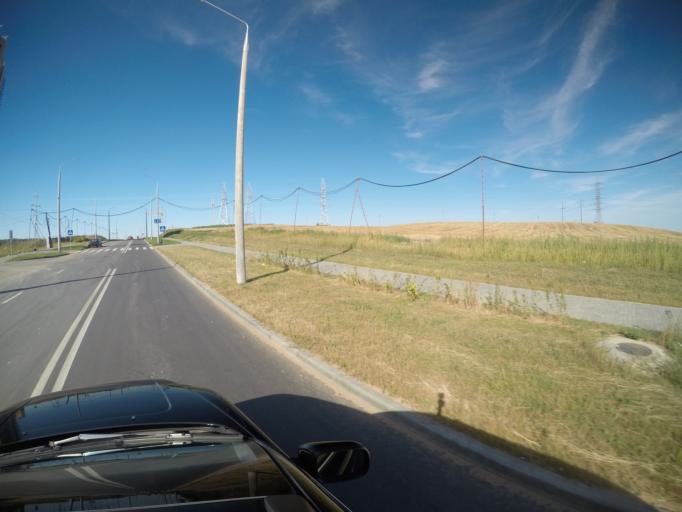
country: BY
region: Grodnenskaya
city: Hrodna
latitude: 53.7175
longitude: 23.8693
